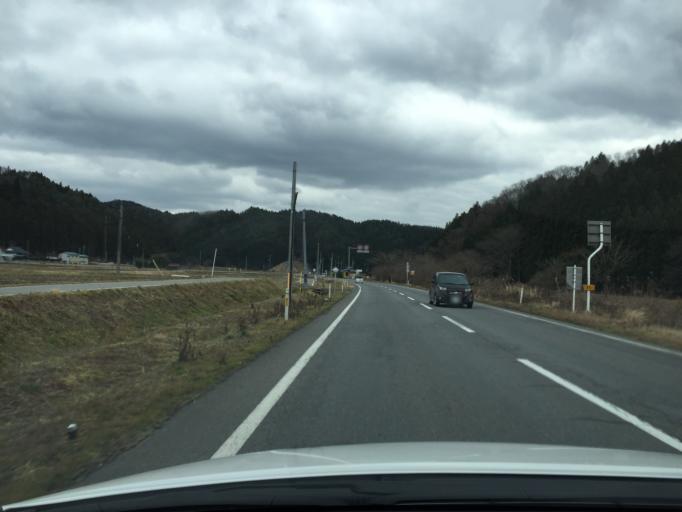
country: JP
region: Fukushima
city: Iwaki
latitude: 37.1332
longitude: 140.7126
